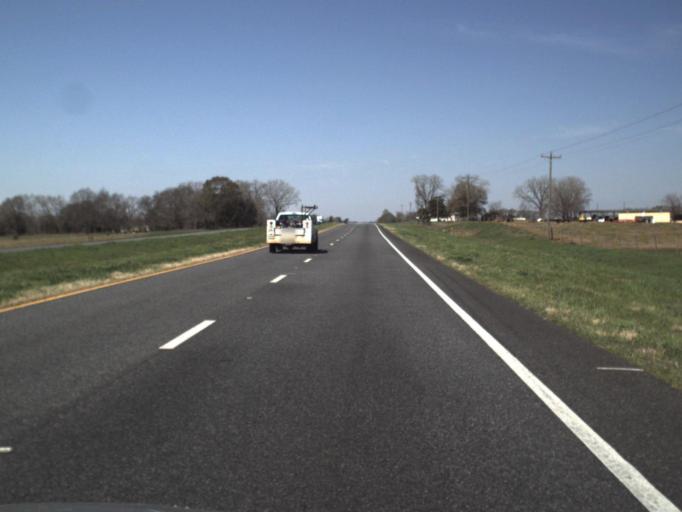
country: US
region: Florida
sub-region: Jackson County
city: Graceville
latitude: 30.8910
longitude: -85.3692
